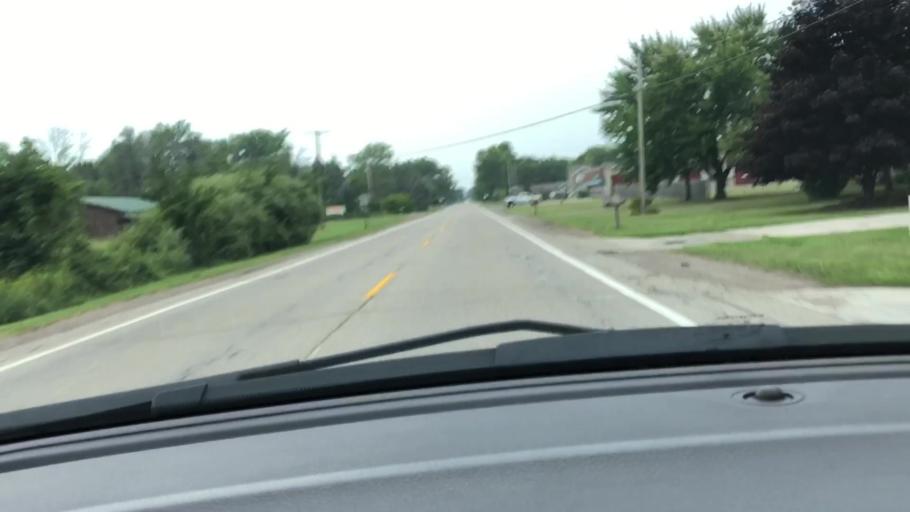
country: US
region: Michigan
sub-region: Bay County
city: Auburn
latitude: 43.6042
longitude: -84.1267
